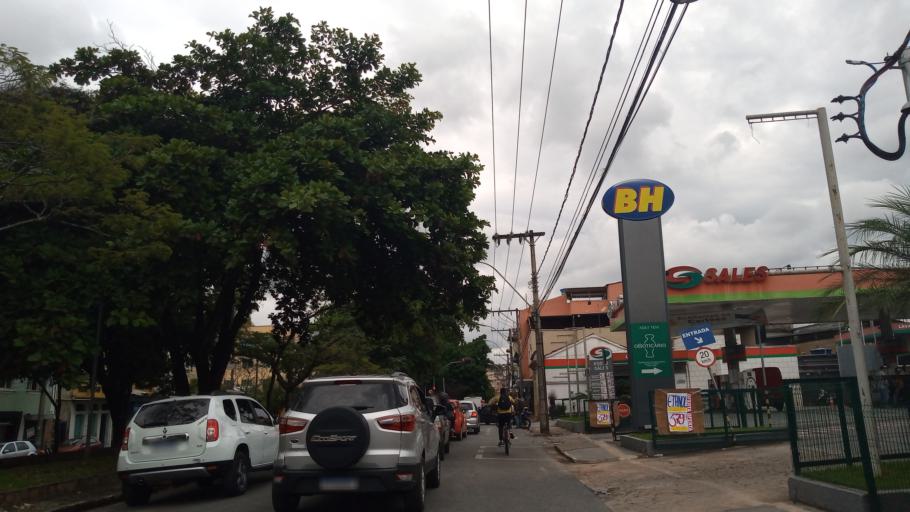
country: BR
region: Minas Gerais
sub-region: Sao Joao Del Rei
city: Sao Joao del Rei
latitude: -21.1275
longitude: -44.2496
